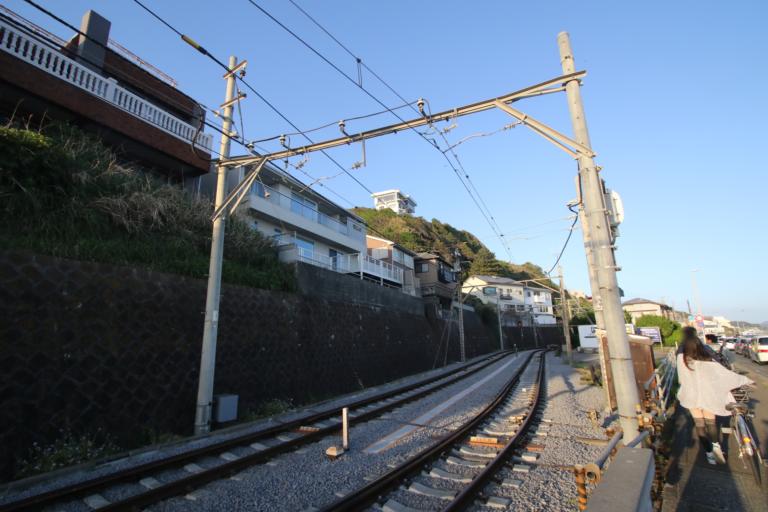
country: JP
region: Kanagawa
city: Kamakura
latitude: 35.3063
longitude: 139.5048
